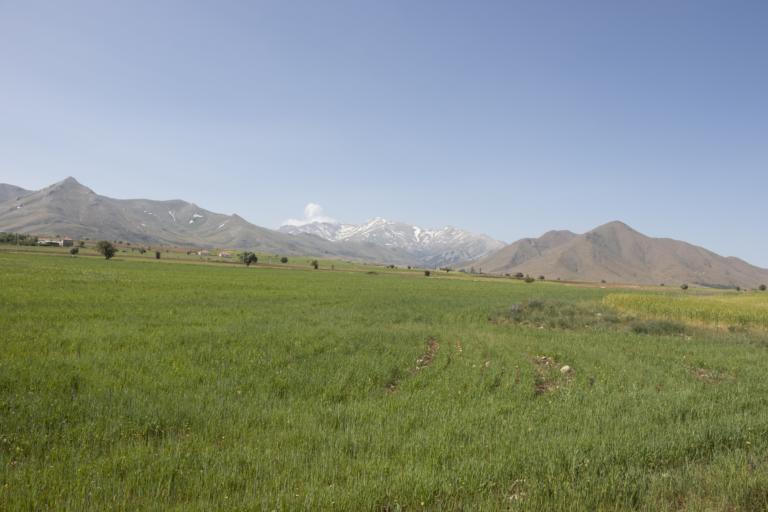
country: TR
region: Kayseri
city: Toklar
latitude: 38.4286
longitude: 36.0881
